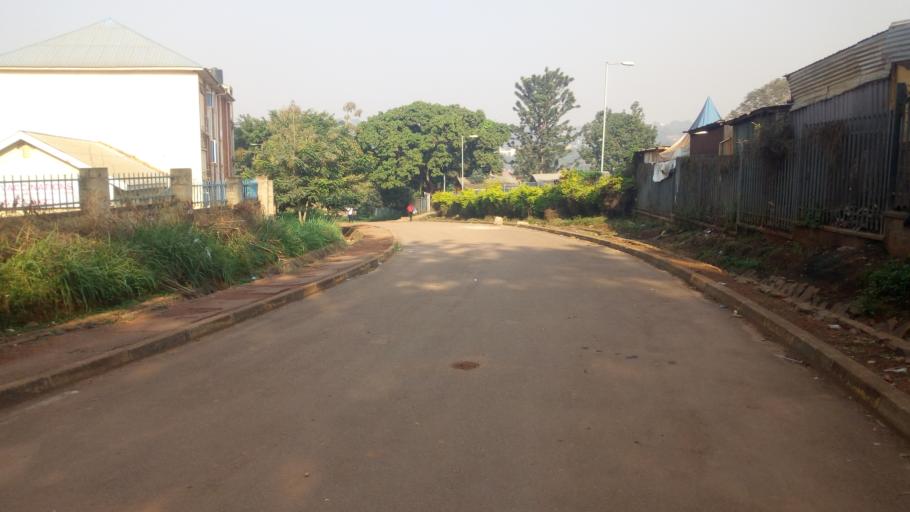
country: UG
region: Central Region
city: Kampala Central Division
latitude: 0.3358
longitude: 32.5773
